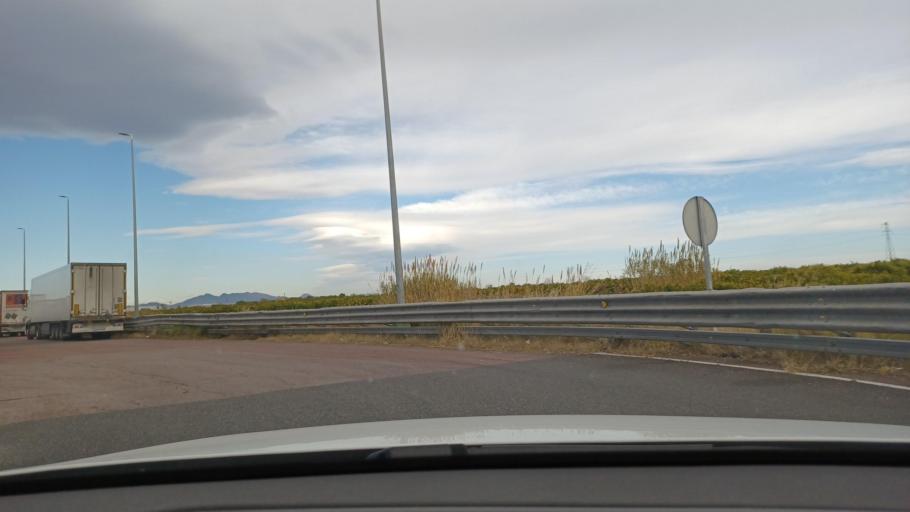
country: ES
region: Valencia
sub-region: Provincia de Castello
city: Alquerias del Nino Perdido
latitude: 39.8643
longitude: -0.1206
